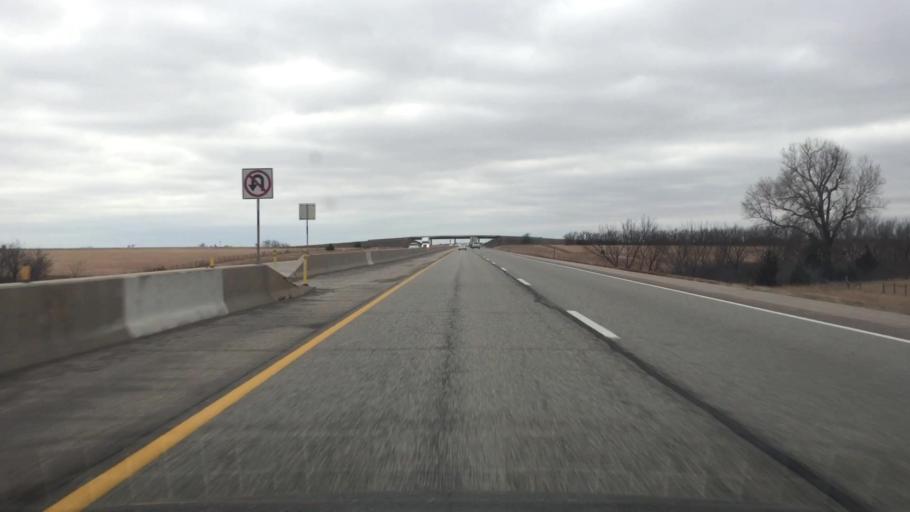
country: US
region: Kansas
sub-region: Butler County
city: El Dorado
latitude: 38.0175
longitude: -96.6720
